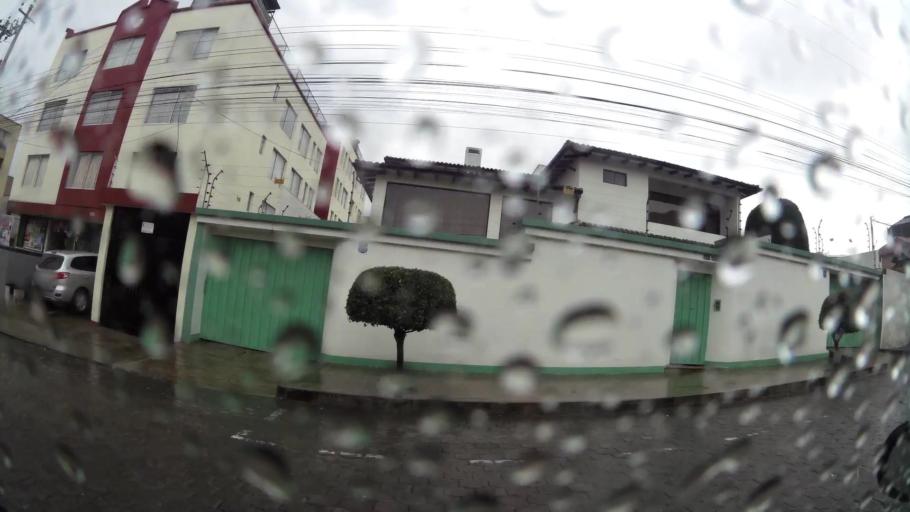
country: EC
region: Pichincha
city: Quito
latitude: -0.1558
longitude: -78.4619
